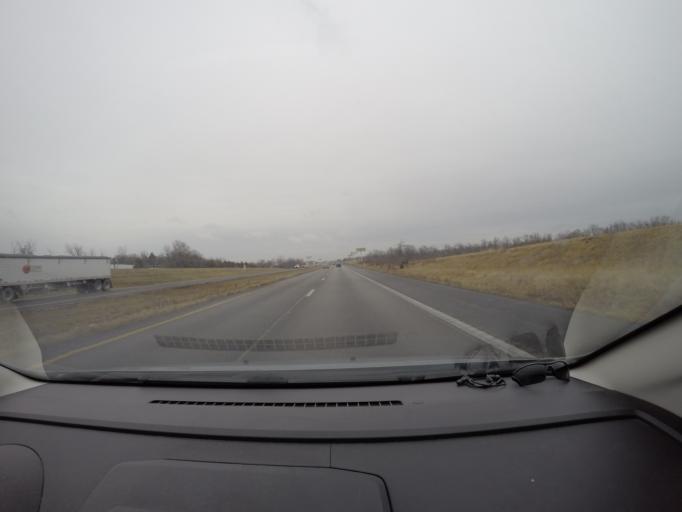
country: US
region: Missouri
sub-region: Warren County
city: Warrenton
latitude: 38.8629
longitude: -91.3208
